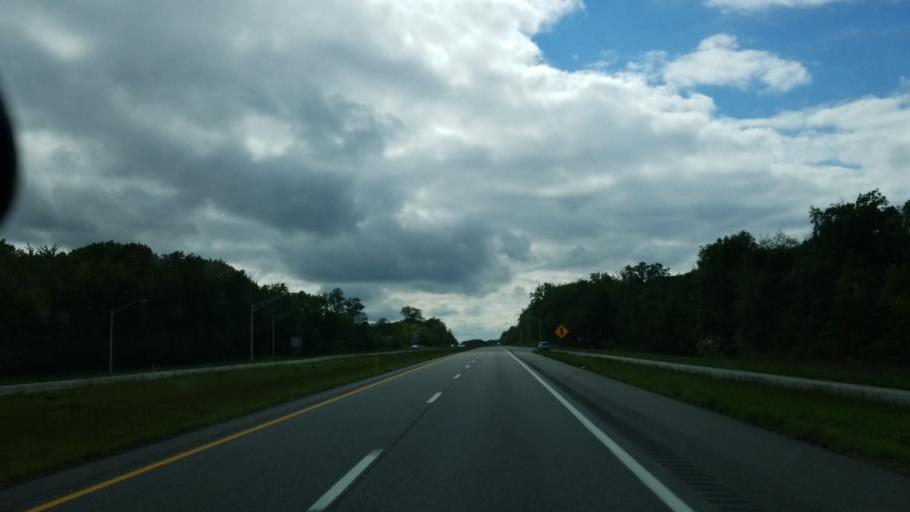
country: US
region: Ohio
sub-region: Portage County
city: Mantua
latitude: 41.3841
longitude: -81.2192
